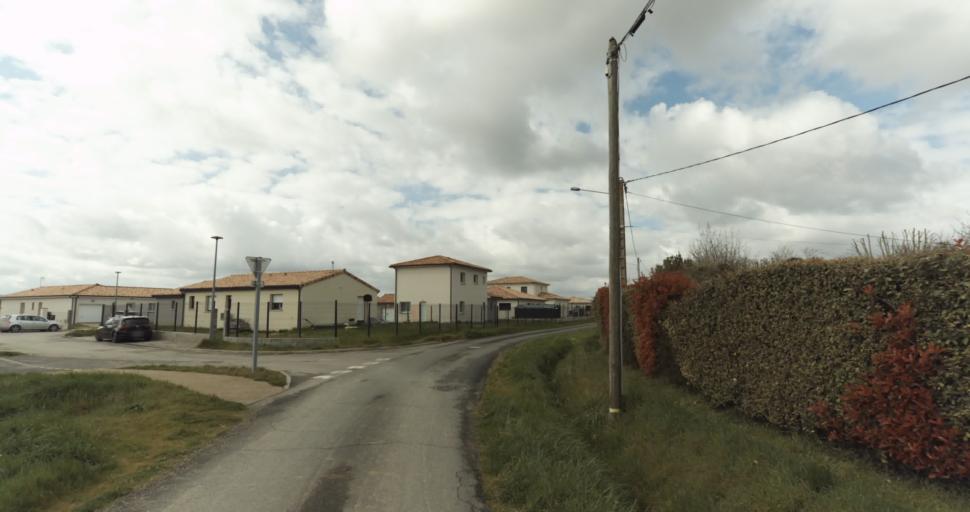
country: FR
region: Midi-Pyrenees
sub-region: Departement de la Haute-Garonne
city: Auterive
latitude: 43.3436
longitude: 1.4580
